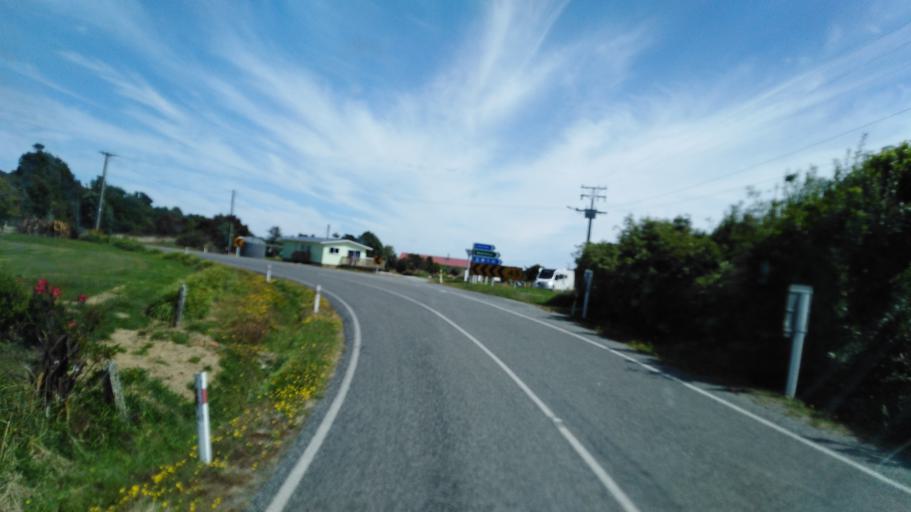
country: NZ
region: West Coast
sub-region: Buller District
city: Westport
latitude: -41.5292
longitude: 171.9448
